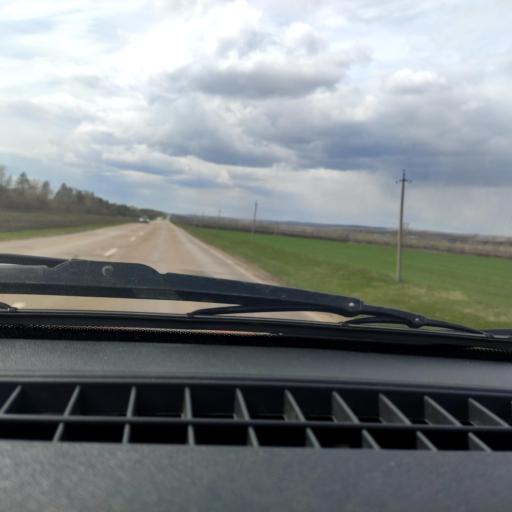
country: RU
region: Bashkortostan
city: Chekmagush
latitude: 55.1087
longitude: 54.9567
